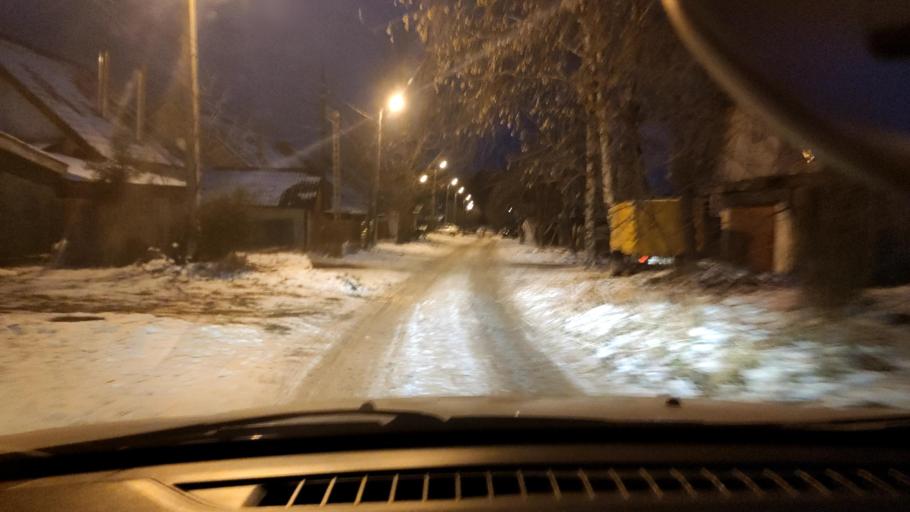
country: RU
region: Perm
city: Kondratovo
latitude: 58.0489
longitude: 56.1078
